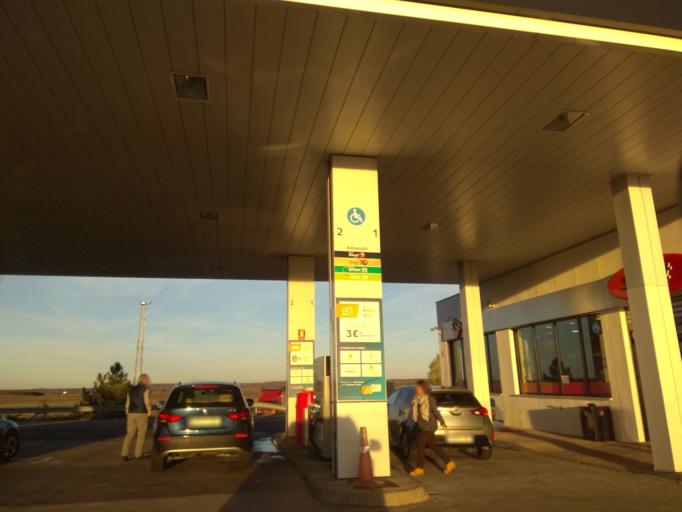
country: ES
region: Castille and Leon
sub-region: Provincia de Salamanca
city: Castraz
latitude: 40.7116
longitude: -6.3877
